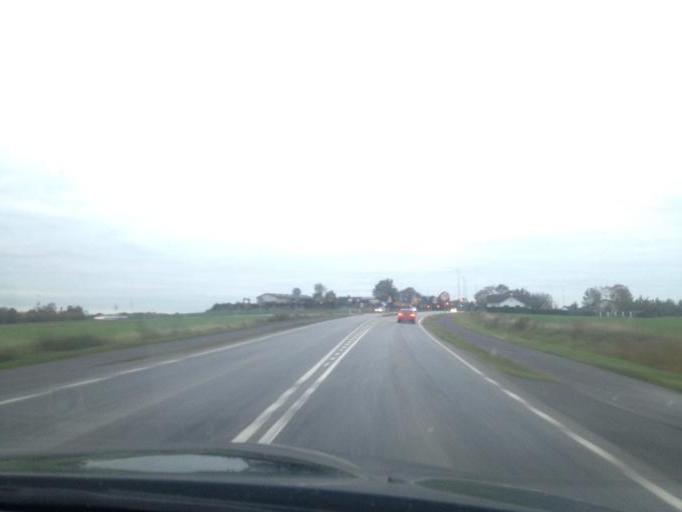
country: DK
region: Zealand
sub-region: Solrod Kommune
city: Havdrup
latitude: 55.5698
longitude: 12.1156
